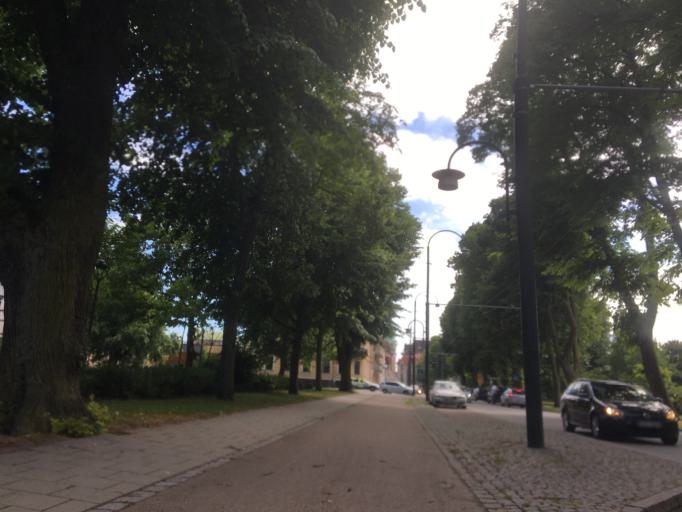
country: SE
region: Skane
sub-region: Landskrona
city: Landskrona
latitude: 55.8730
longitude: 12.8308
